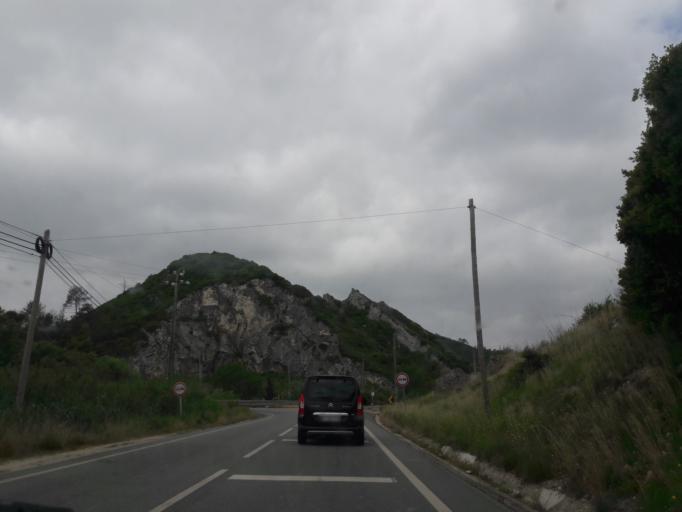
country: PT
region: Leiria
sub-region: Obidos
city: Obidos
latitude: 39.3472
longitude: -9.1878
